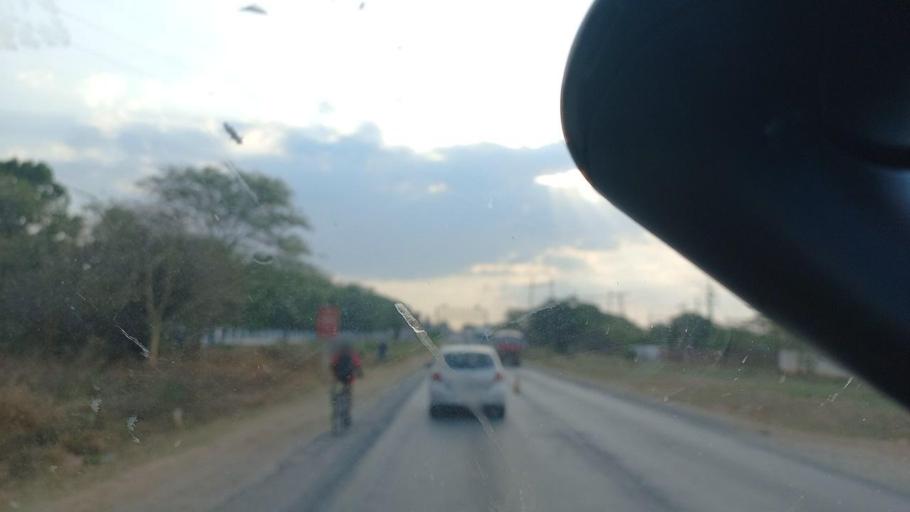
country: ZM
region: Lusaka
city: Lusaka
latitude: -15.3690
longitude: 28.4086
